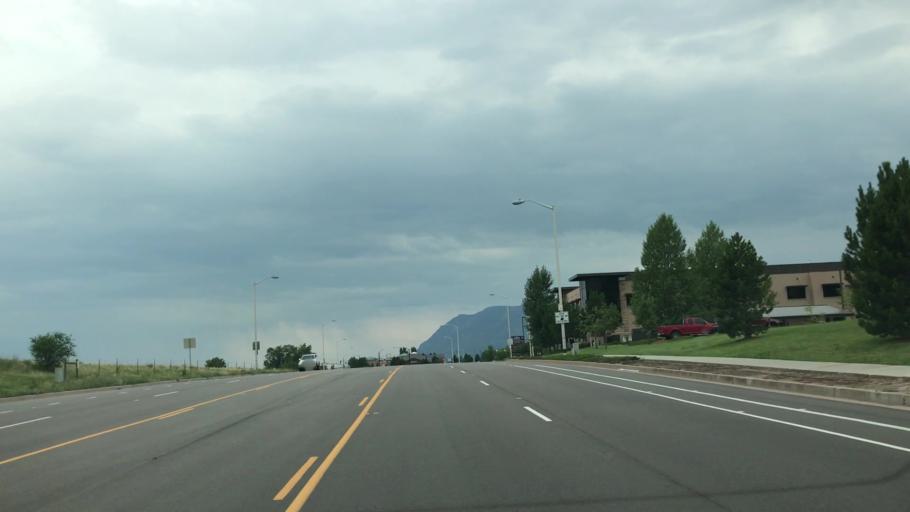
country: US
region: Colorado
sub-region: El Paso County
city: Colorado Springs
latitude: 38.8819
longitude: -104.8477
